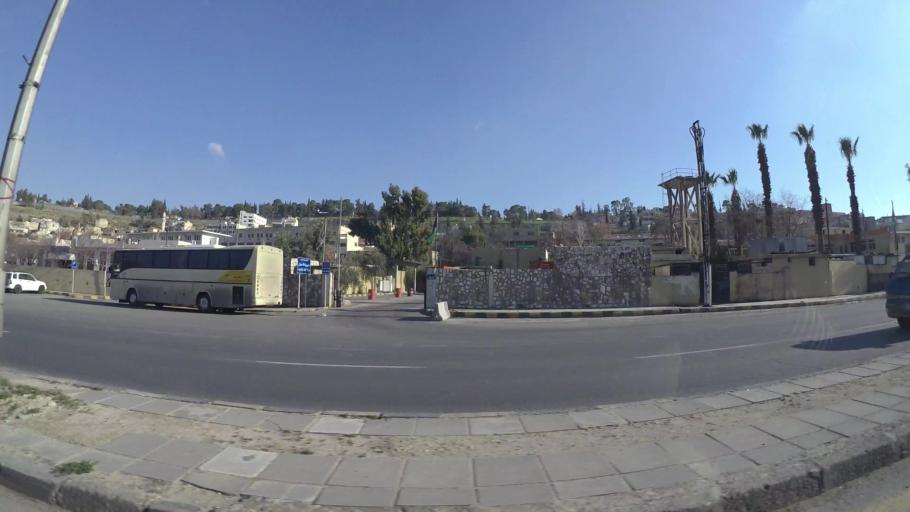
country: JO
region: Amman
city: Amman
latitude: 31.9700
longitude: 35.9677
